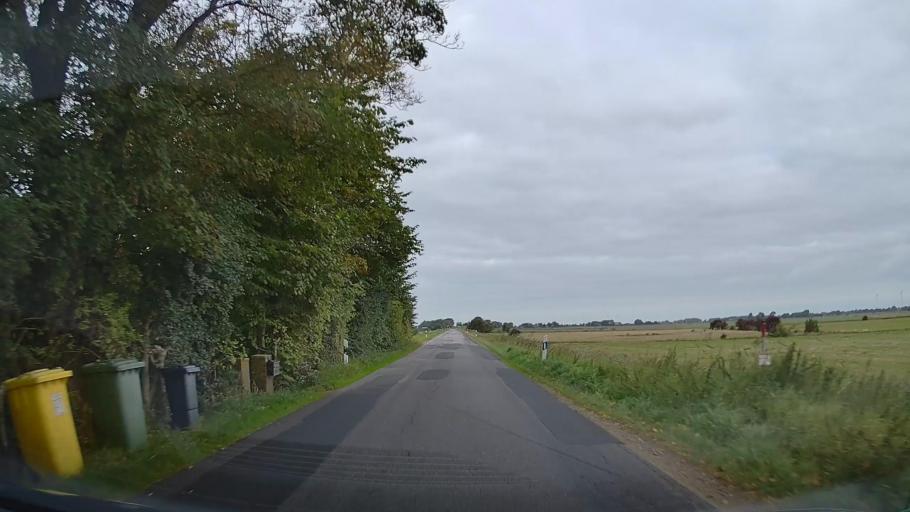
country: DE
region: Schleswig-Holstein
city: Emmelsbull-Horsbull
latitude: 54.7909
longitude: 8.7268
